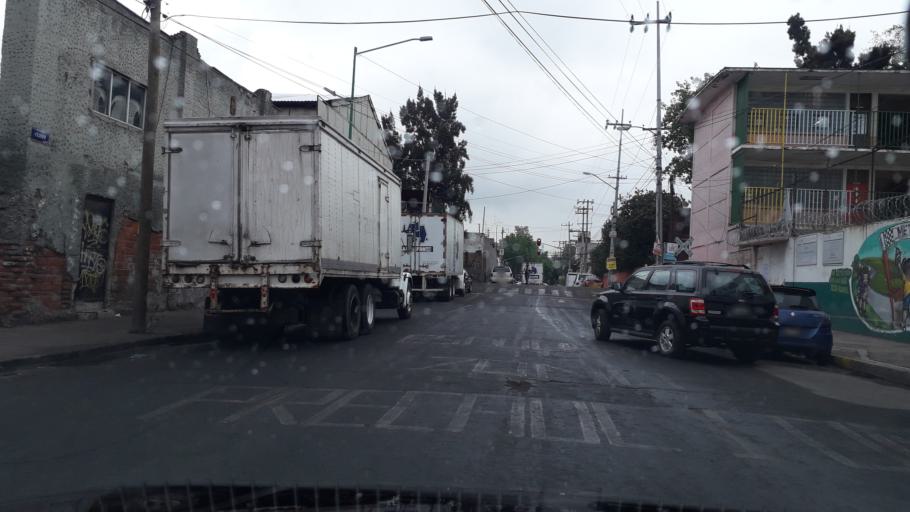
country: MX
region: Mexico City
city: Cuauhtemoc
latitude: 19.4564
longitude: -99.1608
